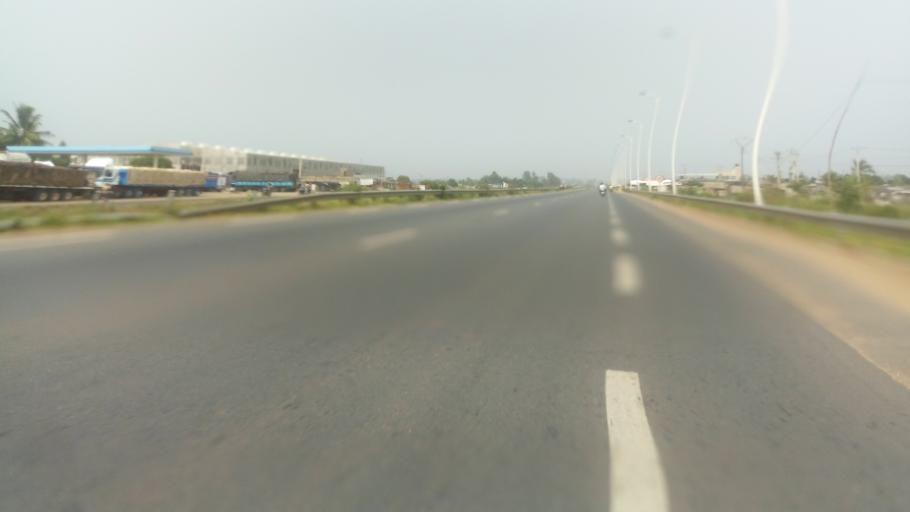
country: TG
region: Maritime
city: Tsevie
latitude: 6.2952
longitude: 1.2137
